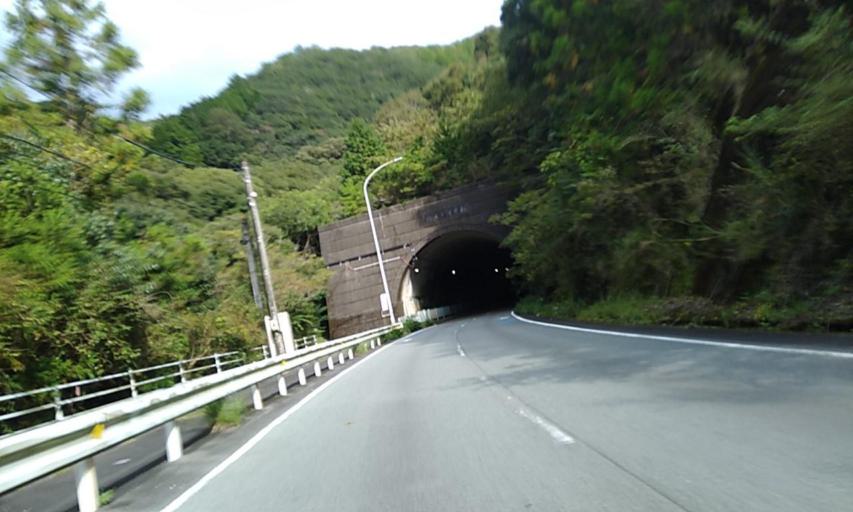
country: JP
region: Mie
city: Ise
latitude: 34.2582
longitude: 136.4750
